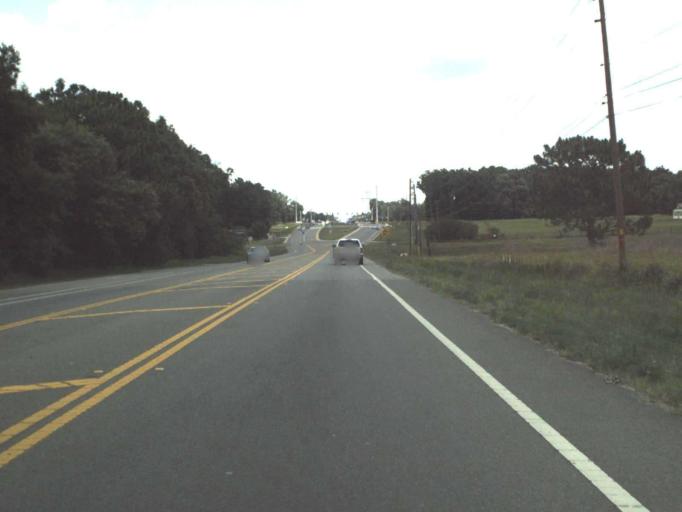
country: US
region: Florida
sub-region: Marion County
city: Silver Springs Shores
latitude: 29.1333
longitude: -82.0536
